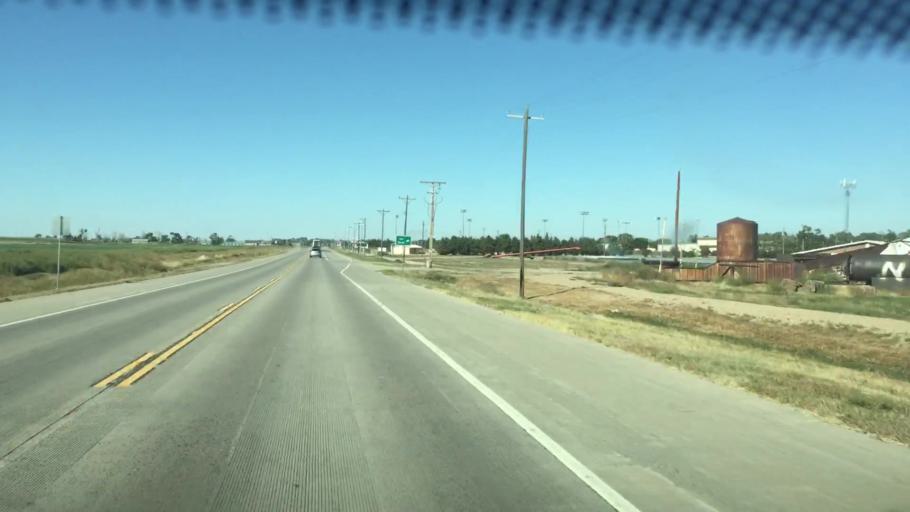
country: US
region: Colorado
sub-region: Prowers County
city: Lamar
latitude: 38.1512
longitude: -102.7236
